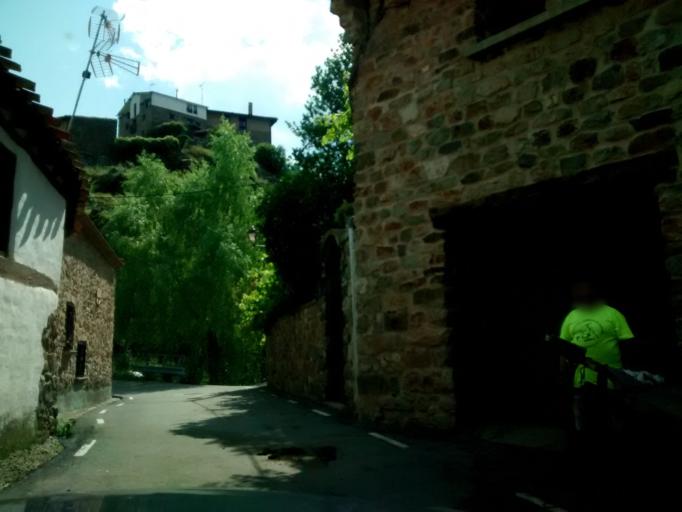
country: ES
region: La Rioja
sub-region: Provincia de La Rioja
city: Ajamil
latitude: 42.1678
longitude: -2.4858
